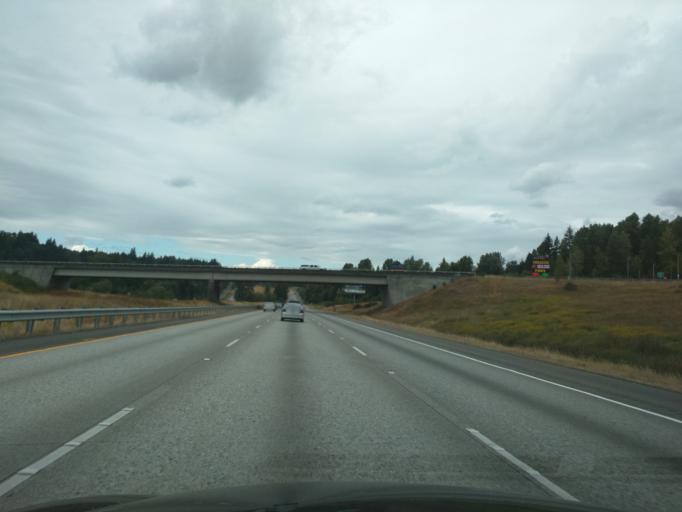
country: US
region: Washington
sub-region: Snohomish County
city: Bryant
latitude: 48.2089
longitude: -122.2154
